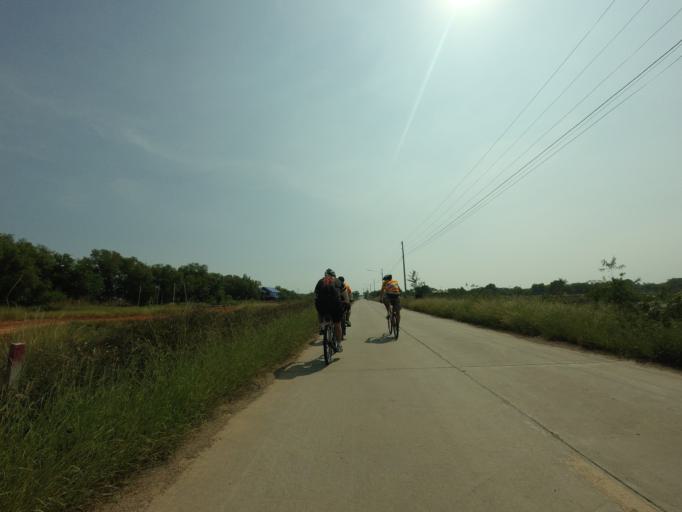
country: TH
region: Samut Sakhon
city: Samut Sakhon
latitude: 13.5030
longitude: 100.3857
